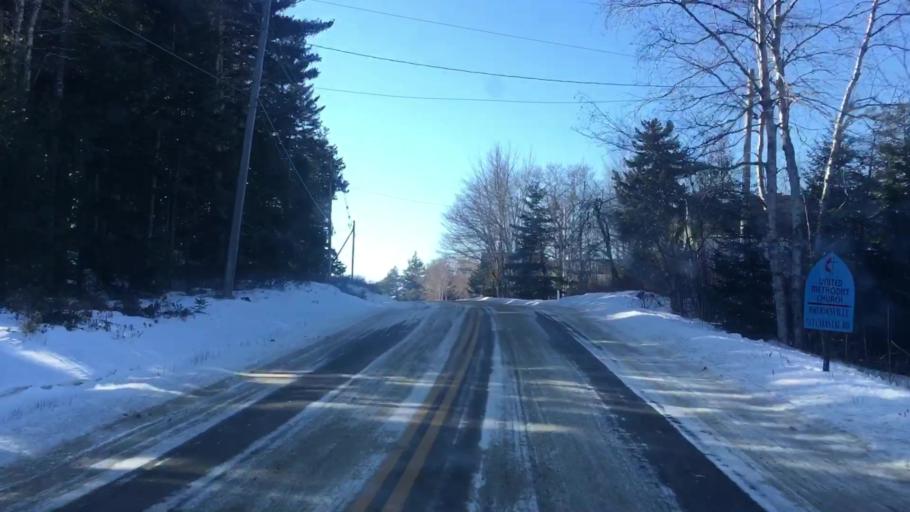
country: US
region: Maine
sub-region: Hancock County
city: Castine
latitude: 44.3406
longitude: -68.7279
